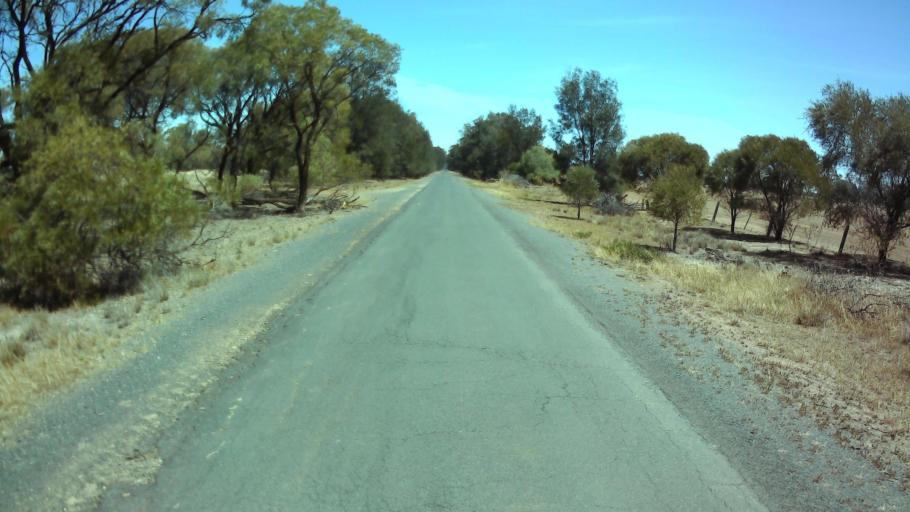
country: AU
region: New South Wales
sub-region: Weddin
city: Grenfell
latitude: -33.8753
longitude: 147.6911
